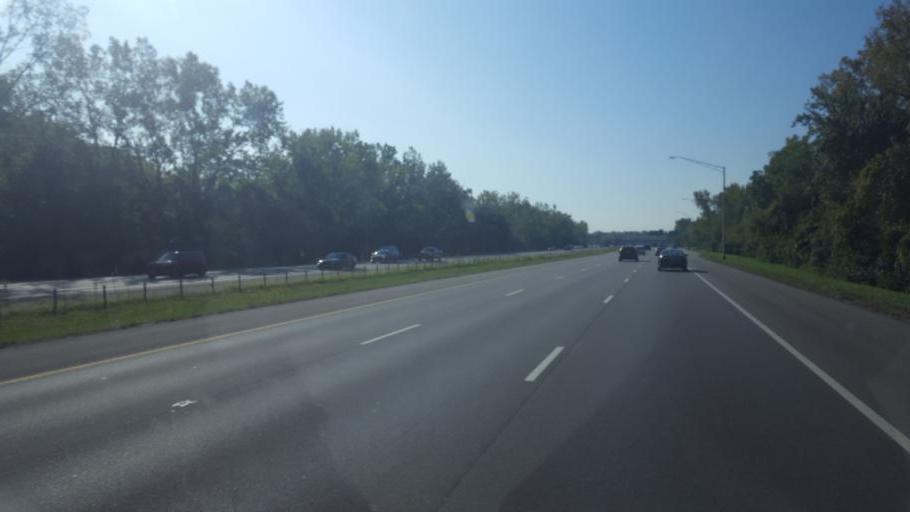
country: US
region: Ohio
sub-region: Franklin County
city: Worthington
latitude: 40.0696
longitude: -83.0345
